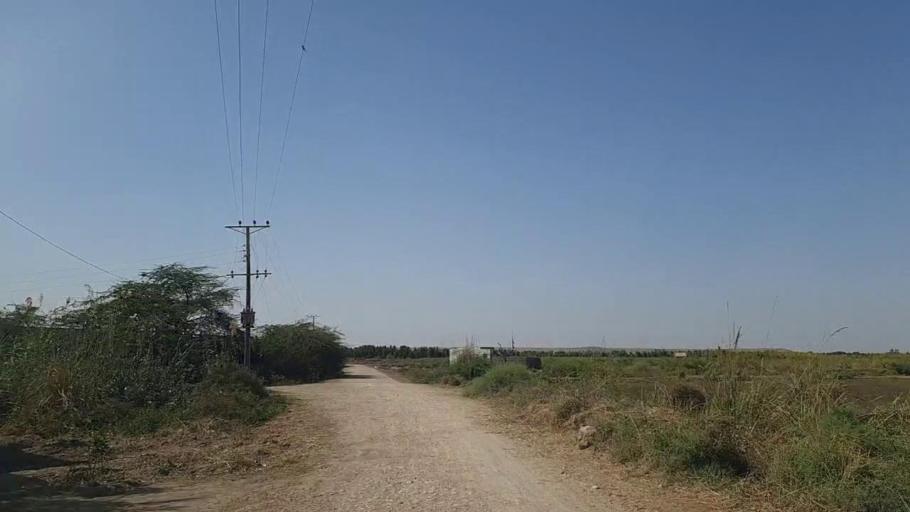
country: PK
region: Sindh
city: Thatta
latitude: 24.6387
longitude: 67.8842
